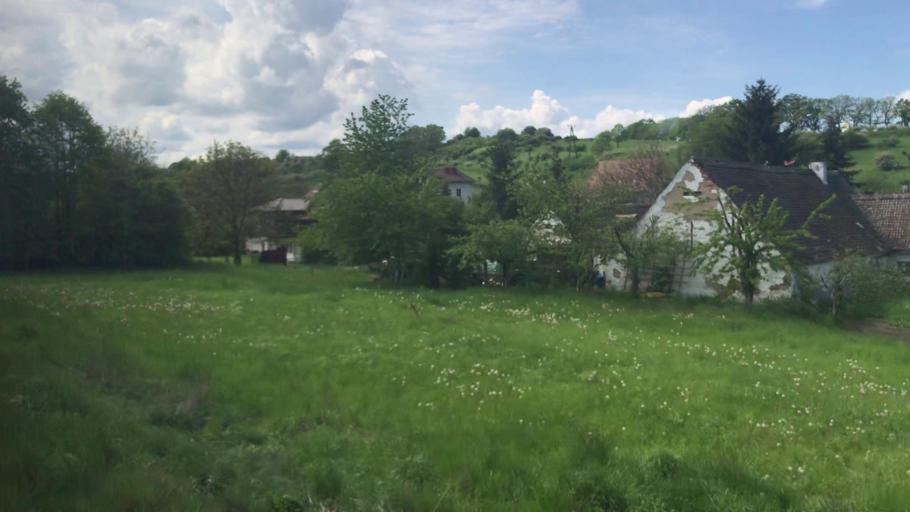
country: PL
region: Lower Silesian Voivodeship
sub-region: Powiat swidnicki
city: Swiebodzice
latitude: 50.8321
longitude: 16.3381
